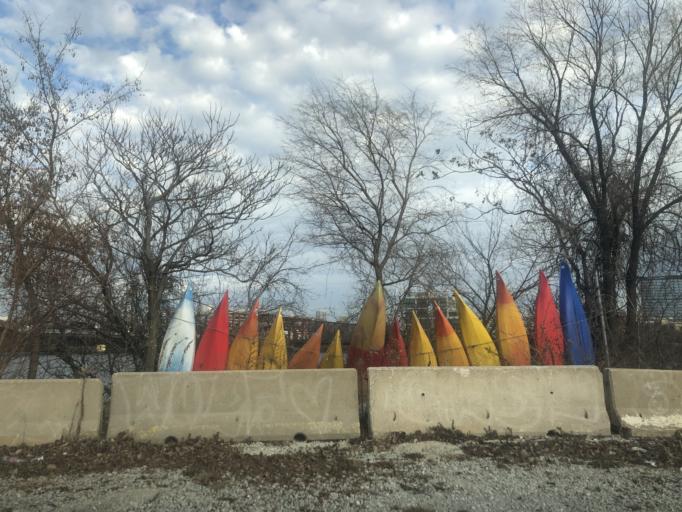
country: US
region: Illinois
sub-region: Cook County
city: Chicago
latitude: 41.9091
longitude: -87.6582
